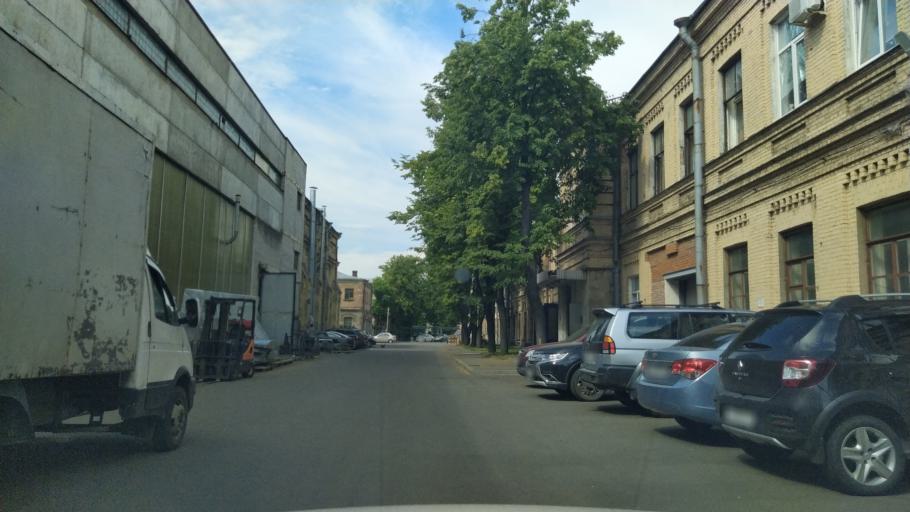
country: RU
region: Leningrad
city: Finlyandskiy
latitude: 59.9599
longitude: 30.3627
